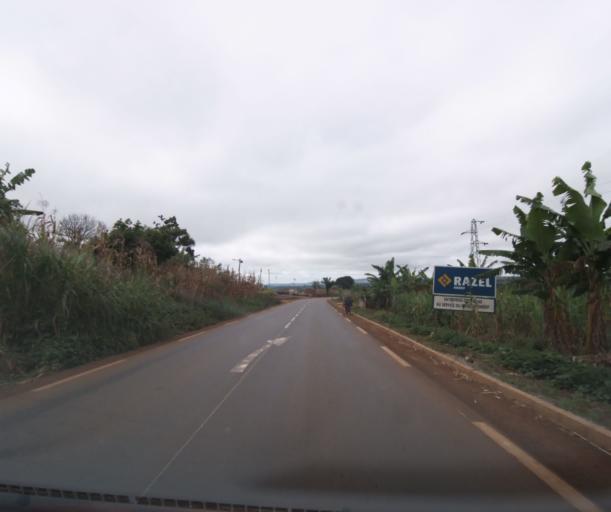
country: CM
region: West
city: Bansoa
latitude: 5.5465
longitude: 10.3283
